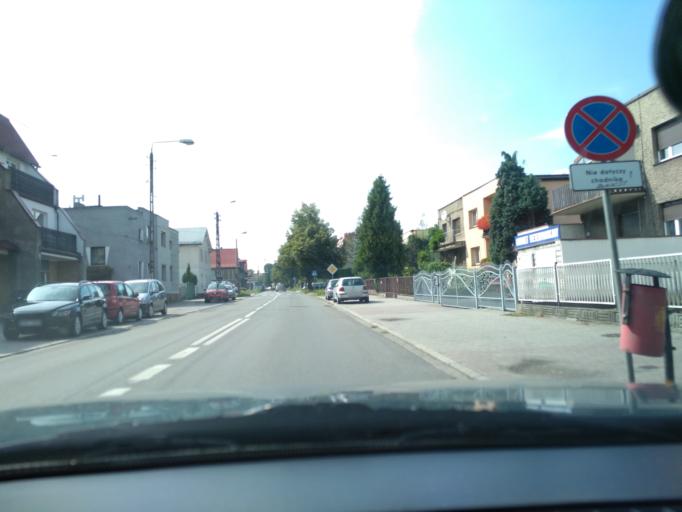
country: PL
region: Silesian Voivodeship
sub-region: Powiat raciborski
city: Raciborz
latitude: 50.0827
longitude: 18.2039
